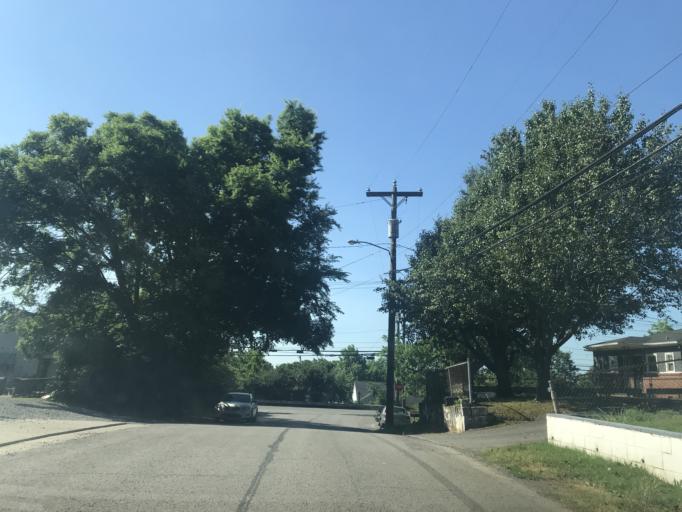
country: US
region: Tennessee
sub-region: Davidson County
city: Nashville
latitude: 36.1865
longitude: -86.8072
